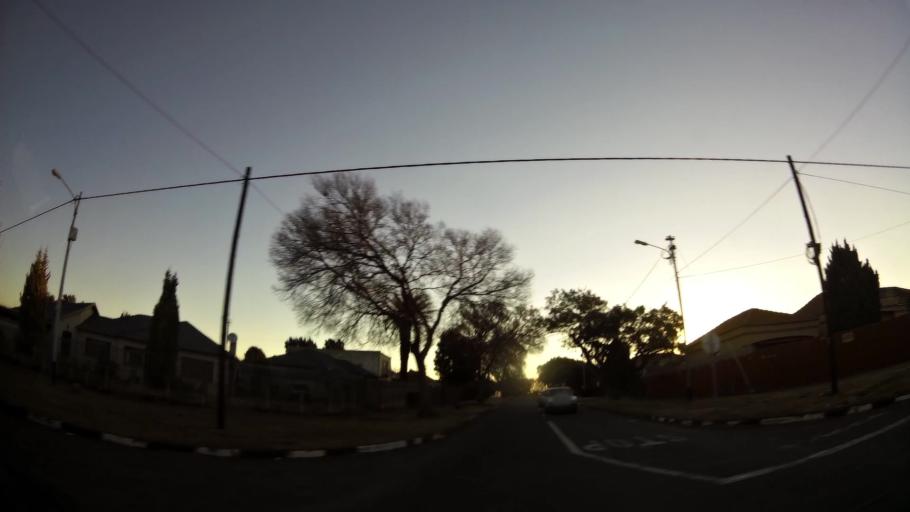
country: ZA
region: Gauteng
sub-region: City of Johannesburg Metropolitan Municipality
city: Roodepoort
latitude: -26.1522
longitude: 27.8817
